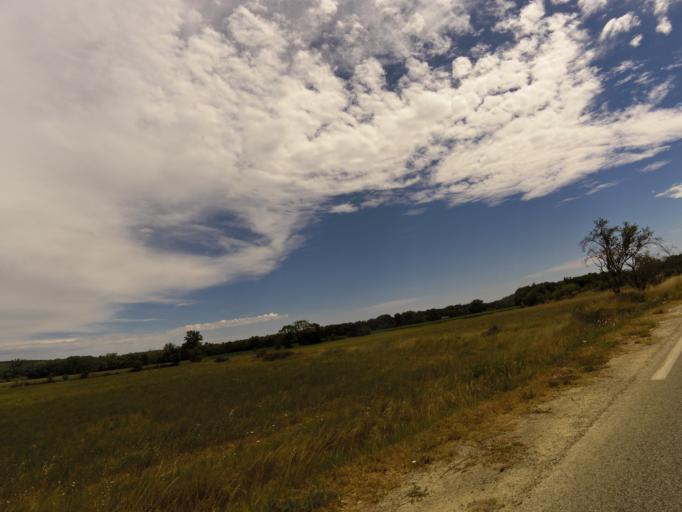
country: FR
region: Languedoc-Roussillon
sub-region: Departement du Gard
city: Quissac
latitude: 43.8848
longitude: 4.0065
